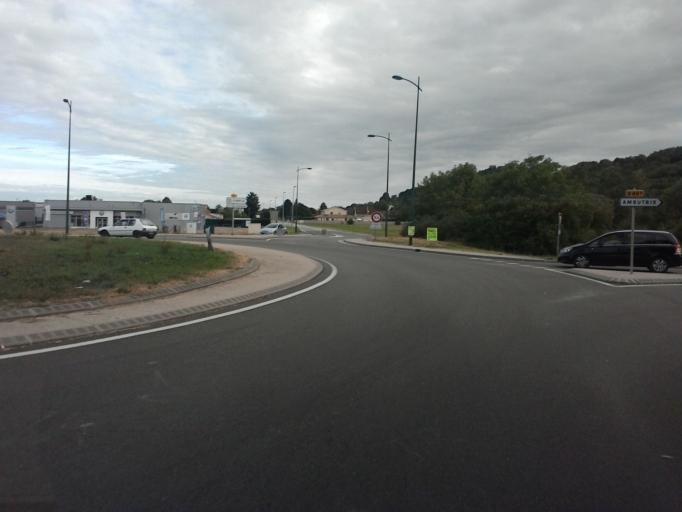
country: FR
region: Rhone-Alpes
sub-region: Departement de l'Ain
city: Saint-Denis-en-Bugey
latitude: 45.9409
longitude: 5.3320
